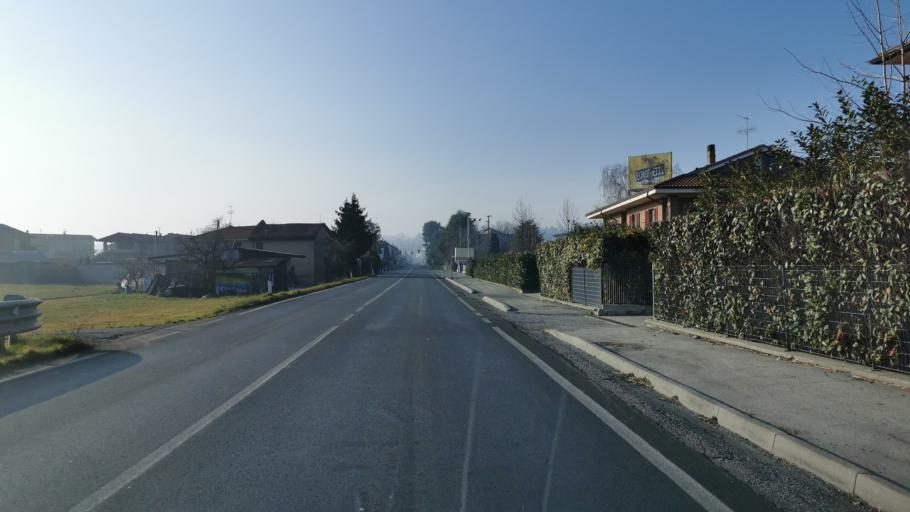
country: IT
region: Piedmont
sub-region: Provincia di Cuneo
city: Pocapaglia
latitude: 44.6967
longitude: 7.8916
